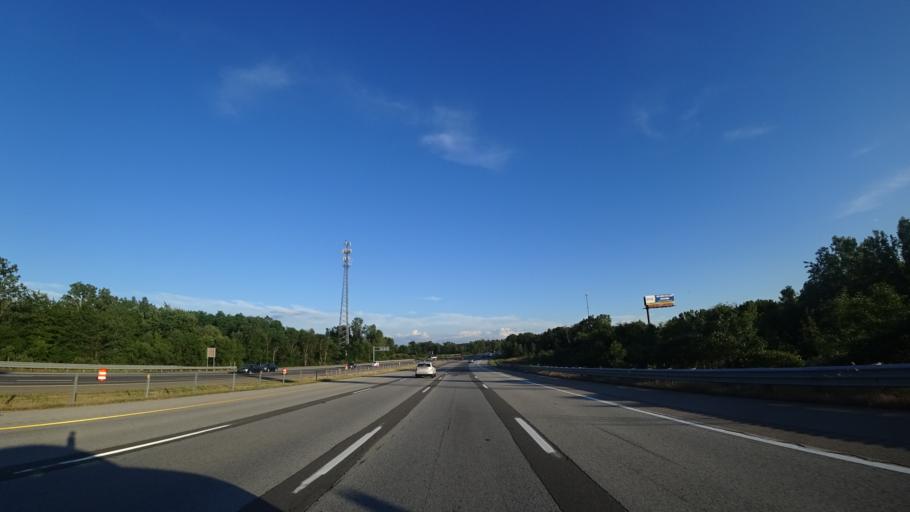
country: US
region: Michigan
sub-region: Berrien County
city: Bridgman
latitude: 41.9282
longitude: -86.5712
